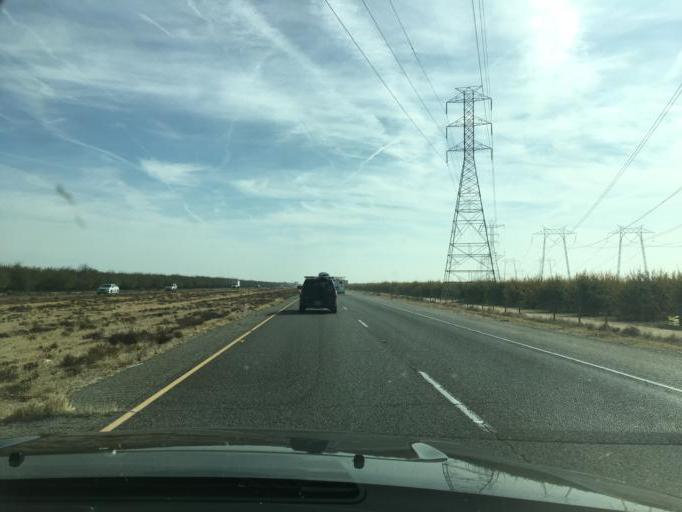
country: US
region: California
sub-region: Kern County
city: Buttonwillow
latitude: 35.4925
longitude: -119.5261
